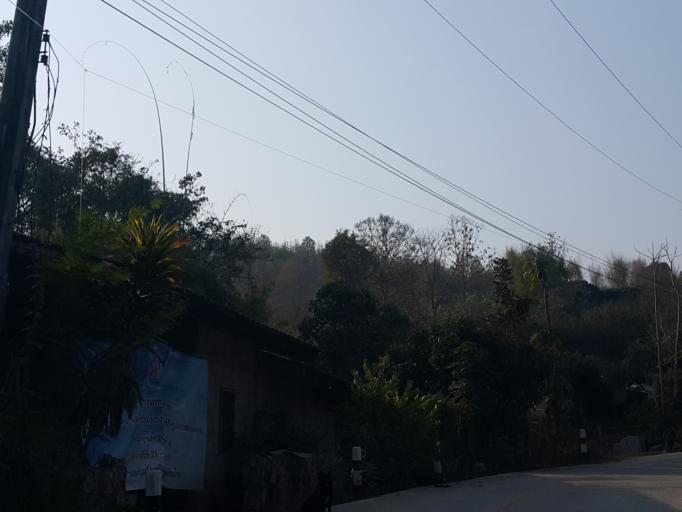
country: TH
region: Chiang Mai
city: Hang Dong
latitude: 18.7543
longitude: 98.8670
